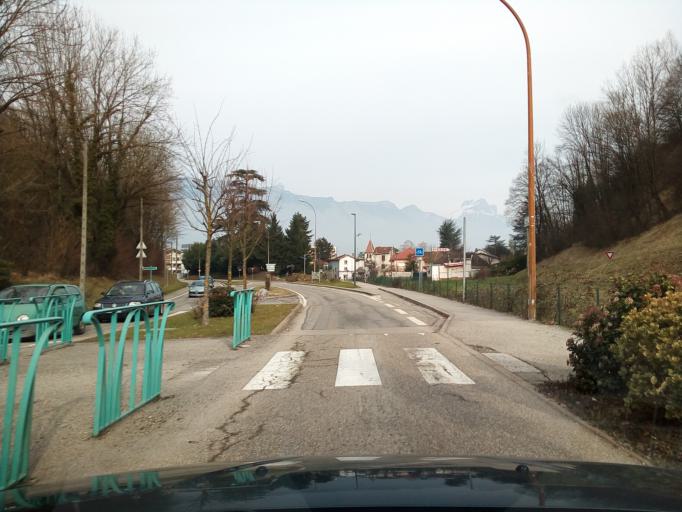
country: FR
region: Rhone-Alpes
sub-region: Departement de l'Isere
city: Gieres
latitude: 45.1772
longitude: 5.7900
